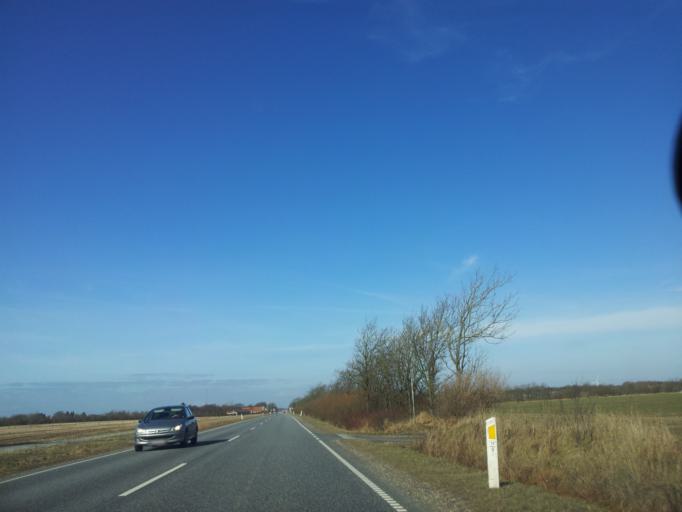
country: DK
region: South Denmark
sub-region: Tonder Kommune
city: Sherrebek
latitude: 55.2268
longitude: 8.7251
